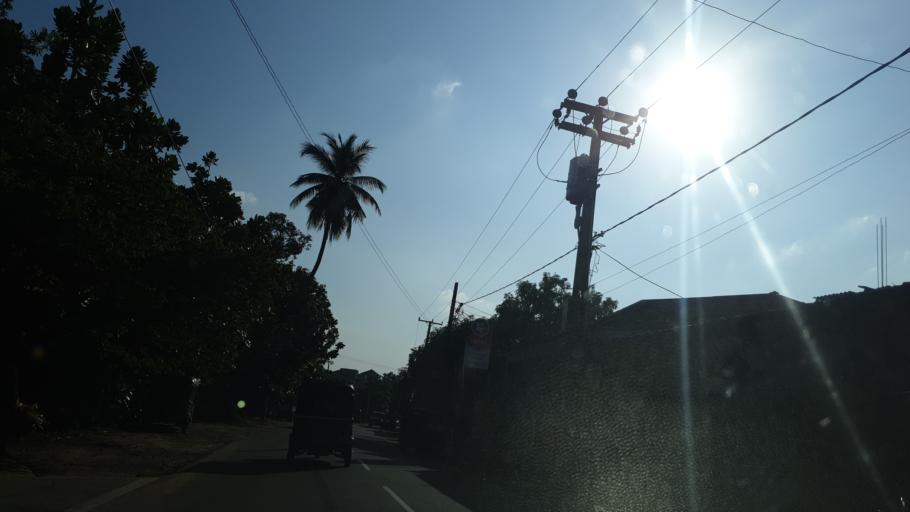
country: LK
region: Western
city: Sri Jayewardenepura Kotte
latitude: 6.8778
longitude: 79.9212
